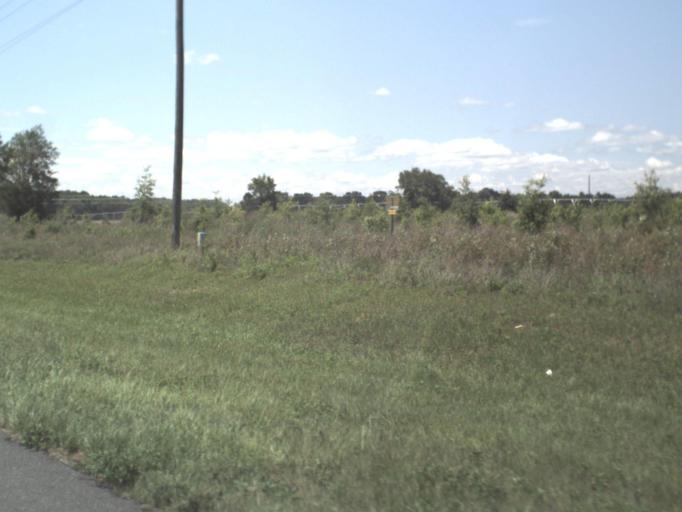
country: US
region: Florida
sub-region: Lafayette County
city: Mayo
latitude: 30.0836
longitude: -83.2200
